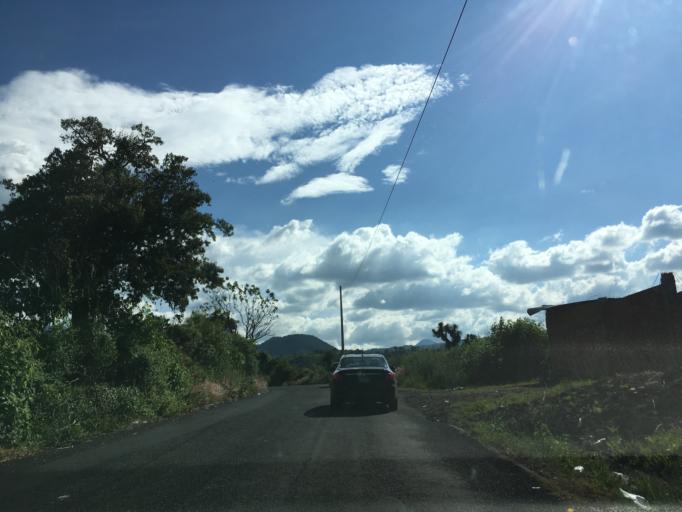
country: MX
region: Michoacan
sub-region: Zacapu
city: Naranja de Tapia
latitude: 19.7748
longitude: -101.7660
